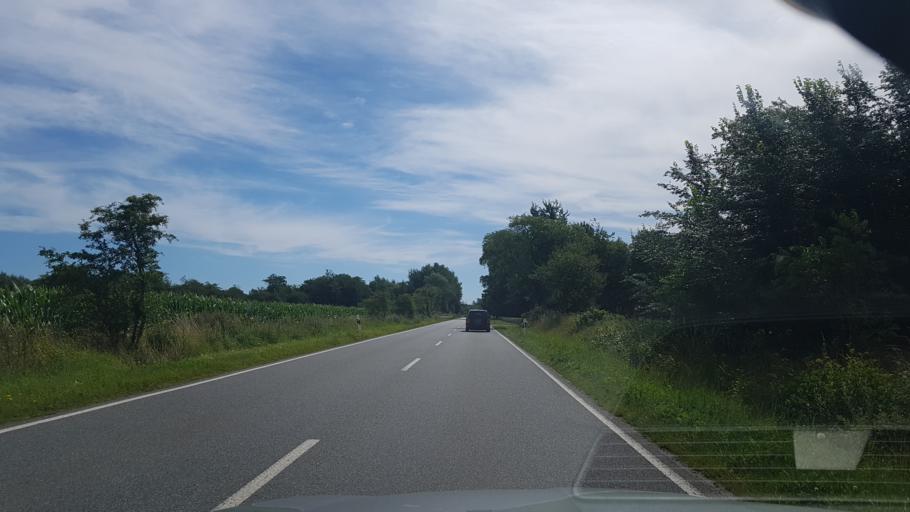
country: DE
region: Schleswig-Holstein
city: Wallsbull
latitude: 54.8009
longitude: 9.2673
